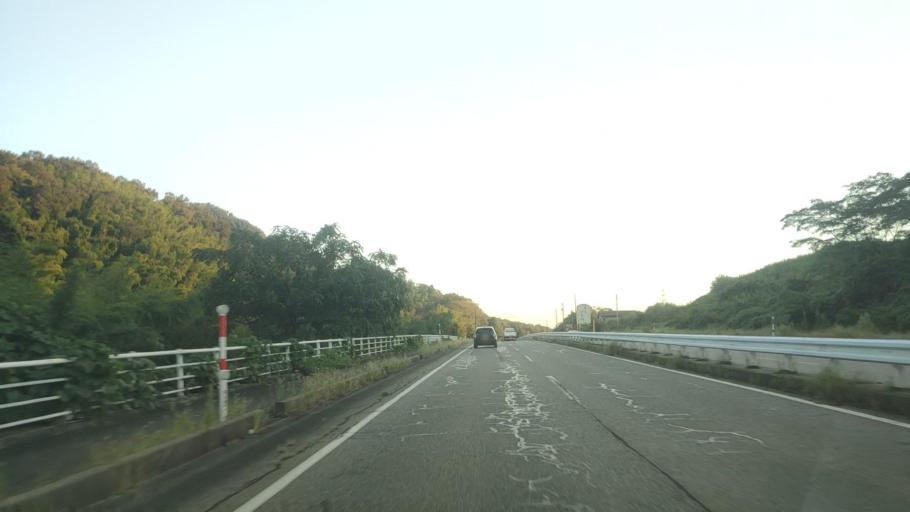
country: JP
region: Toyama
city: Takaoka
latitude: 36.7979
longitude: 137.0019
